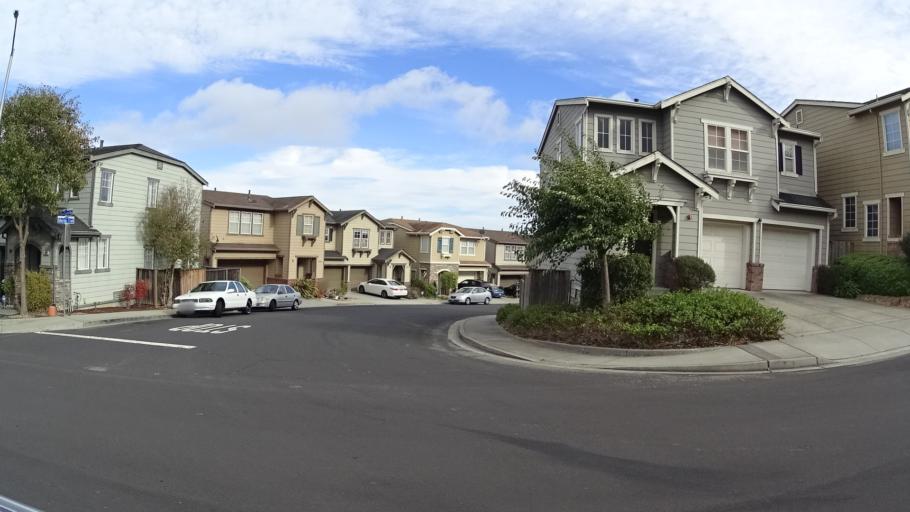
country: US
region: California
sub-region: San Mateo County
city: Brisbane
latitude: 37.7049
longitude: -122.4254
